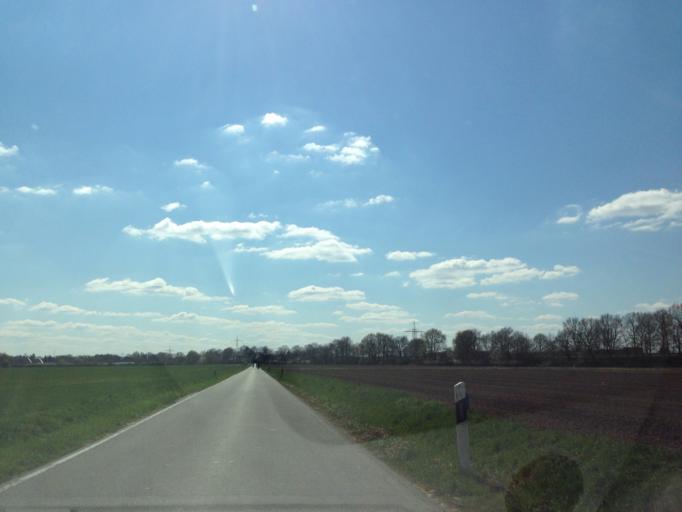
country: DE
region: North Rhine-Westphalia
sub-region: Regierungsbezirk Munster
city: Muenster
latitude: 51.8973
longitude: 7.6039
